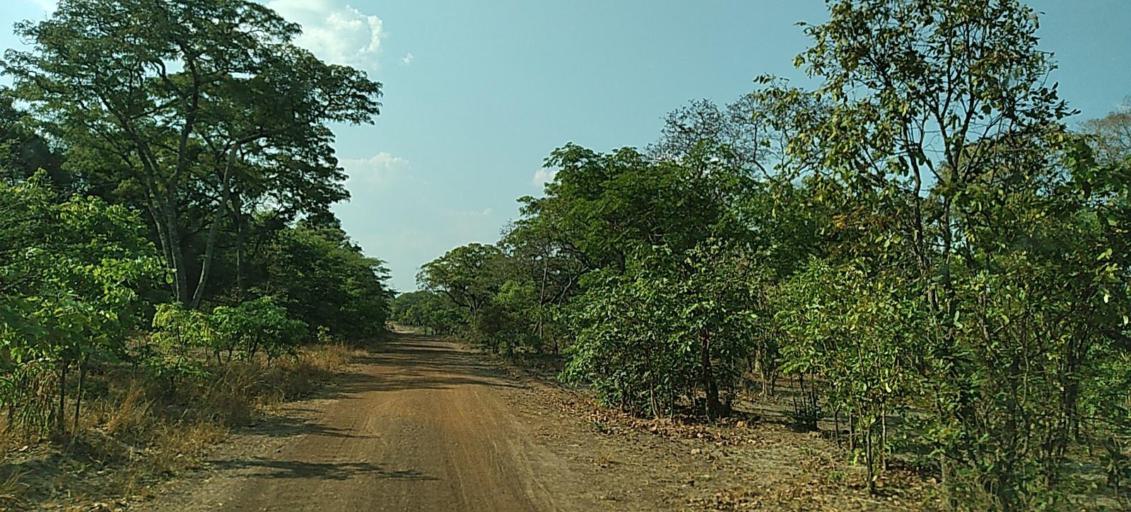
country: ZM
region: Copperbelt
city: Mpongwe
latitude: -13.4426
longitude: 28.0619
